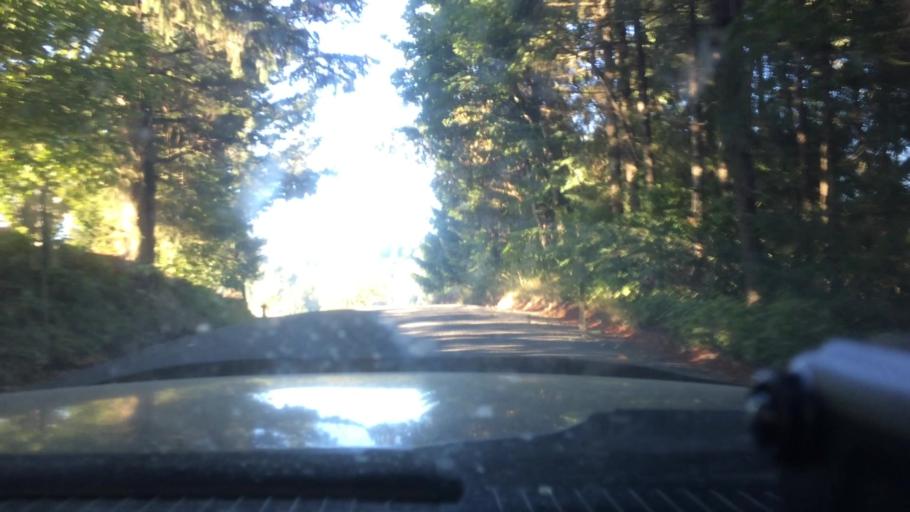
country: US
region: Oregon
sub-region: Yamhill County
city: Newberg
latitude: 45.3718
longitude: -122.9754
